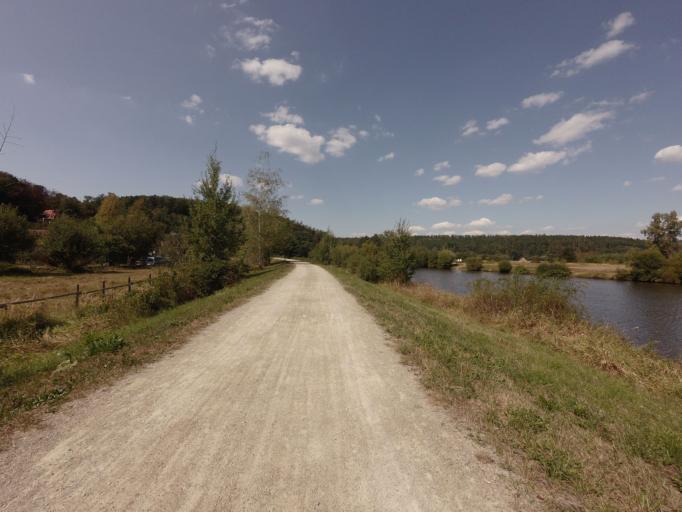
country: CZ
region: Jihocesky
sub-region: Okres Ceske Budejovice
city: Hluboka nad Vltavou
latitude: 49.0554
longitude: 14.4439
